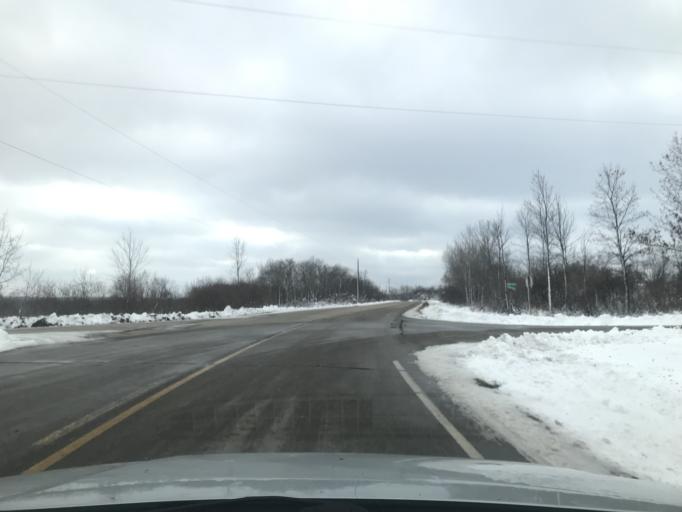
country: US
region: Wisconsin
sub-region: Oconto County
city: Oconto
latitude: 44.9362
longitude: -87.9873
